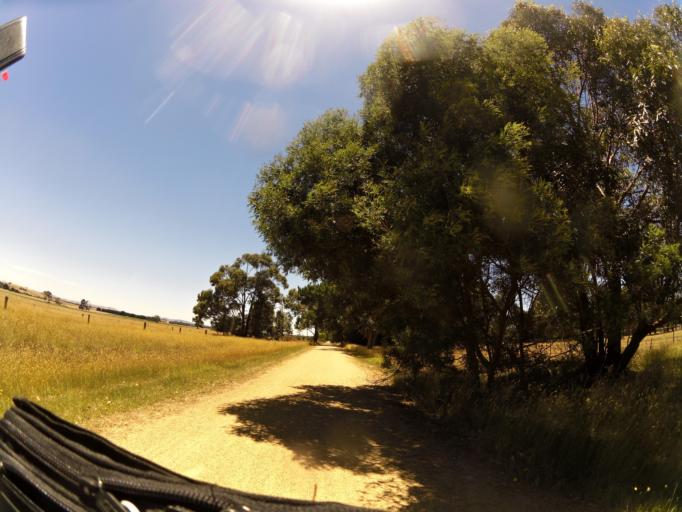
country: AU
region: Victoria
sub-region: Ballarat North
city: Delacombe
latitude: -37.5704
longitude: 143.7303
